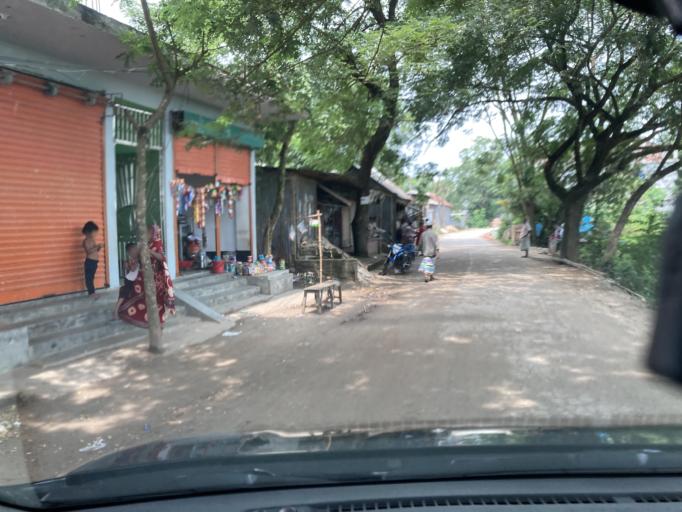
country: BD
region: Dhaka
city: Dohar
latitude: 23.7613
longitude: 90.1973
